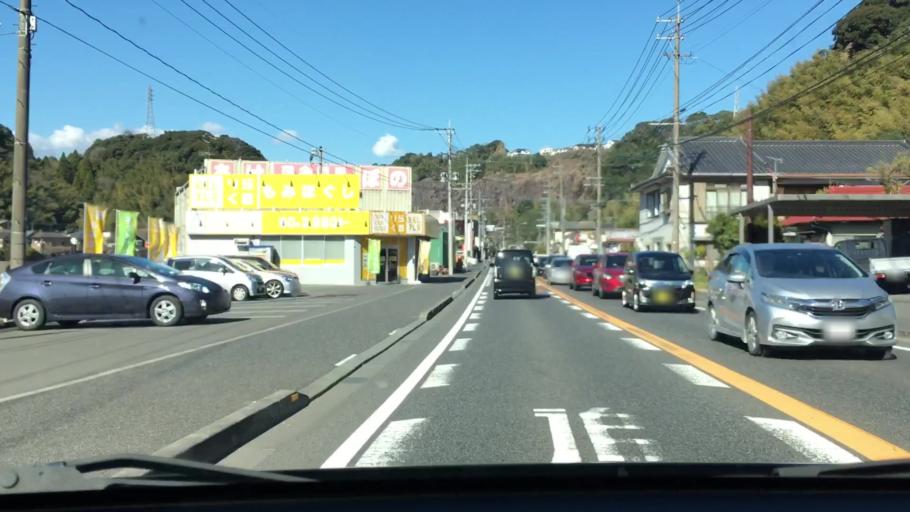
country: JP
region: Kagoshima
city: Kagoshima-shi
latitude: 31.6293
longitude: 130.5249
